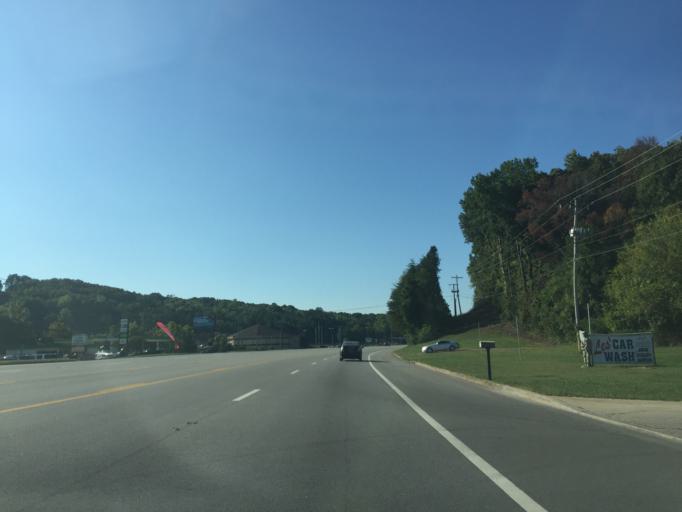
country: US
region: Tennessee
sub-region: Hamilton County
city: Harrison
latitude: 35.1216
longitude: -85.1251
